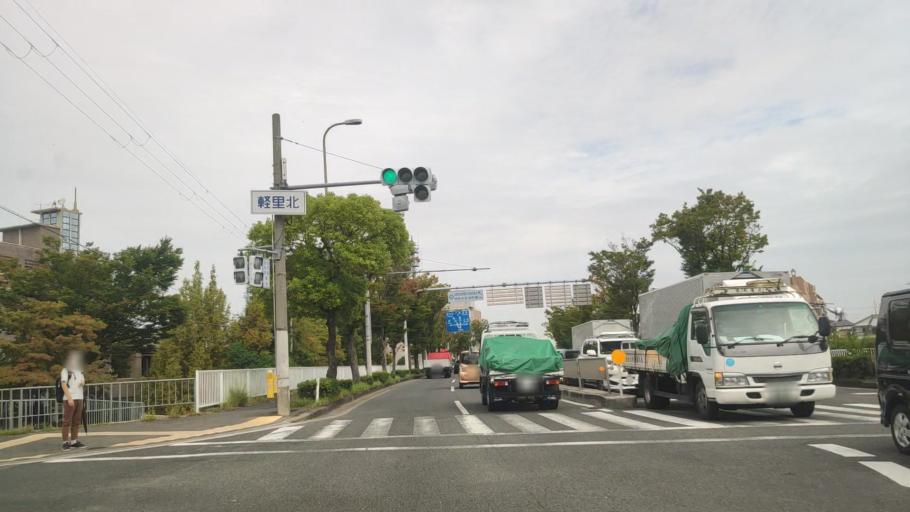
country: JP
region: Osaka
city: Kashihara
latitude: 34.5531
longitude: 135.5990
